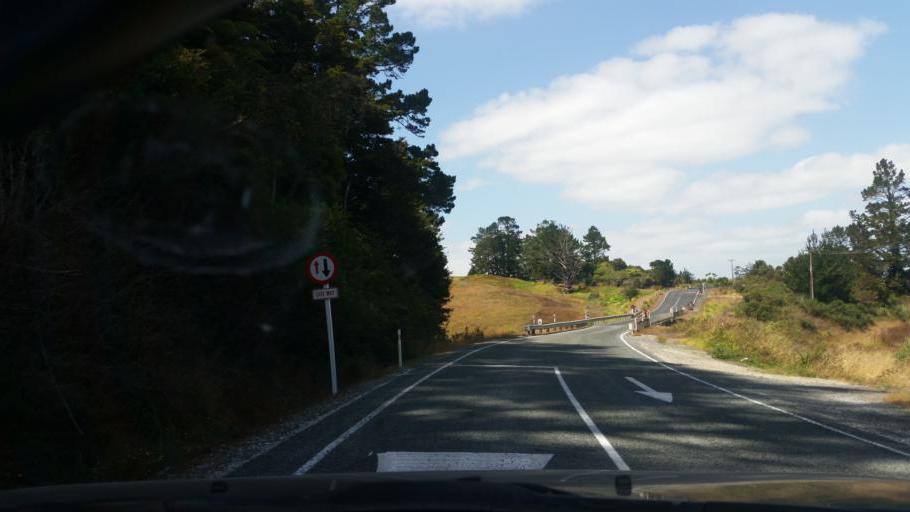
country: NZ
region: Northland
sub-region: Whangarei
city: Ruakaka
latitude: -36.0340
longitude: 174.2790
